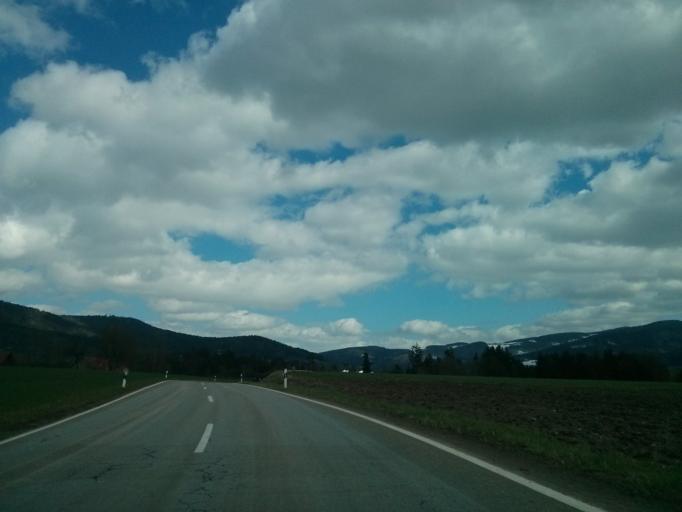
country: DE
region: Bavaria
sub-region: Lower Bavaria
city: Lalling
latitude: 48.8439
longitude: 13.1218
